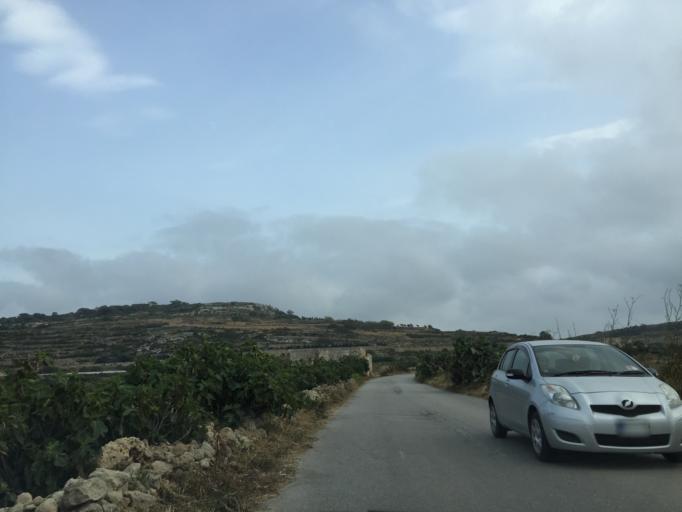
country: MT
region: L-Imgarr
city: Imgarr
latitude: 35.9350
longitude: 14.3512
